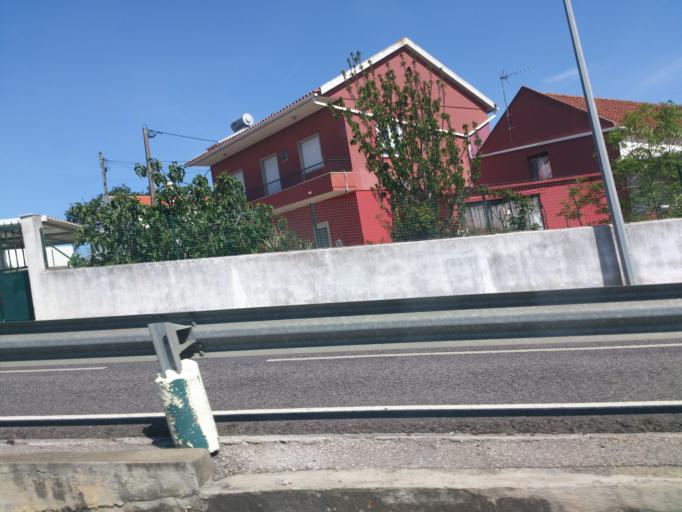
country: PT
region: Lisbon
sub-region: Mafra
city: Mafra
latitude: 38.9358
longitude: -9.3105
